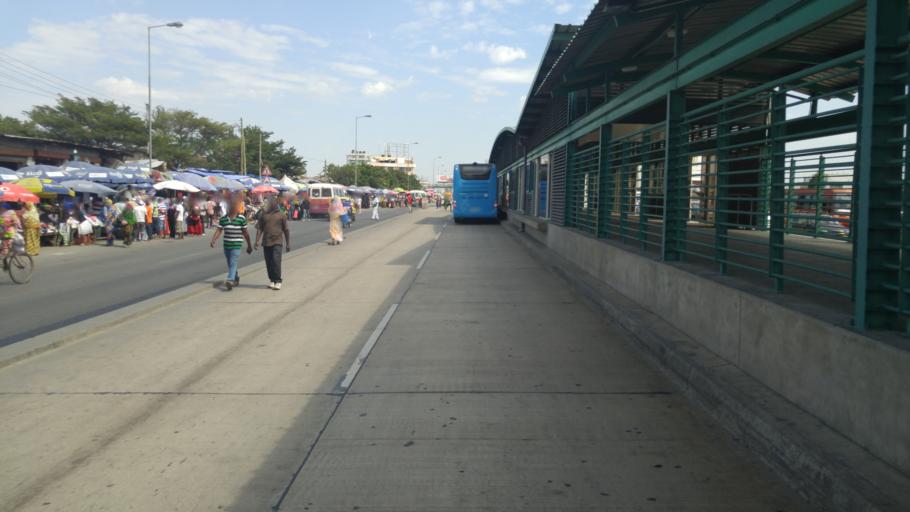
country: TZ
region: Dar es Salaam
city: Magomeni
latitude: -6.7995
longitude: 39.2355
